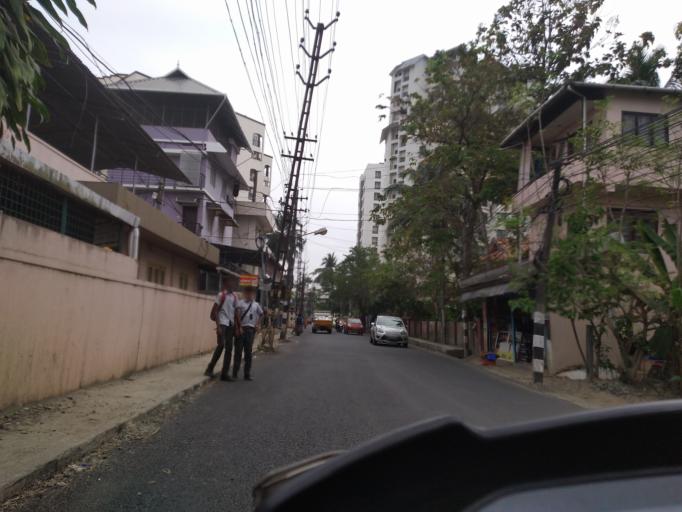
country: IN
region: Kerala
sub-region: Ernakulam
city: Cochin
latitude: 9.9359
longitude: 76.2976
